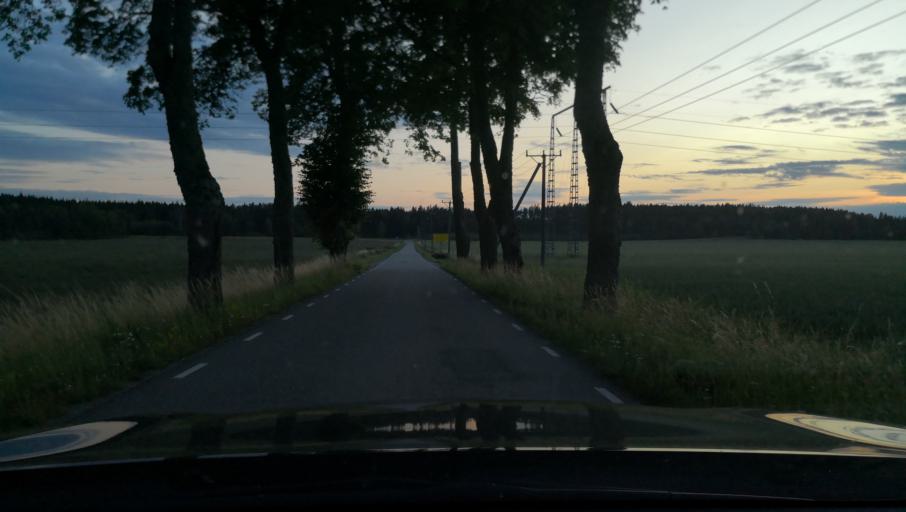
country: SE
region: Uppsala
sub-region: Osthammars Kommun
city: Bjorklinge
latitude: 60.0623
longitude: 17.5544
